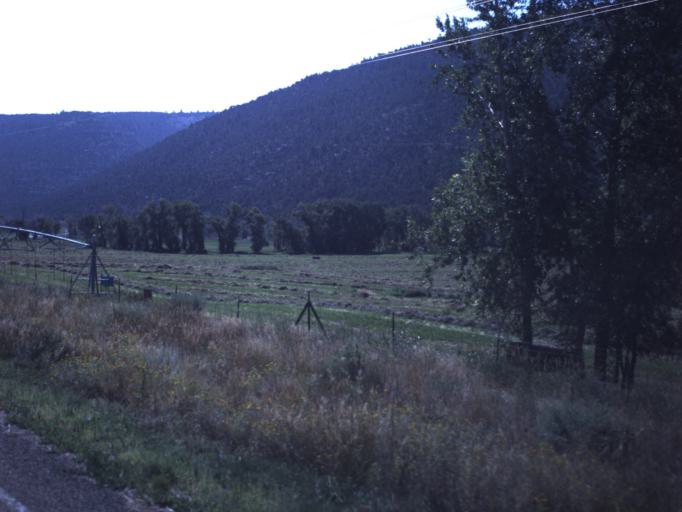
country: US
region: Utah
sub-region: Duchesne County
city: Duchesne
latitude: 40.3029
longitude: -110.6149
